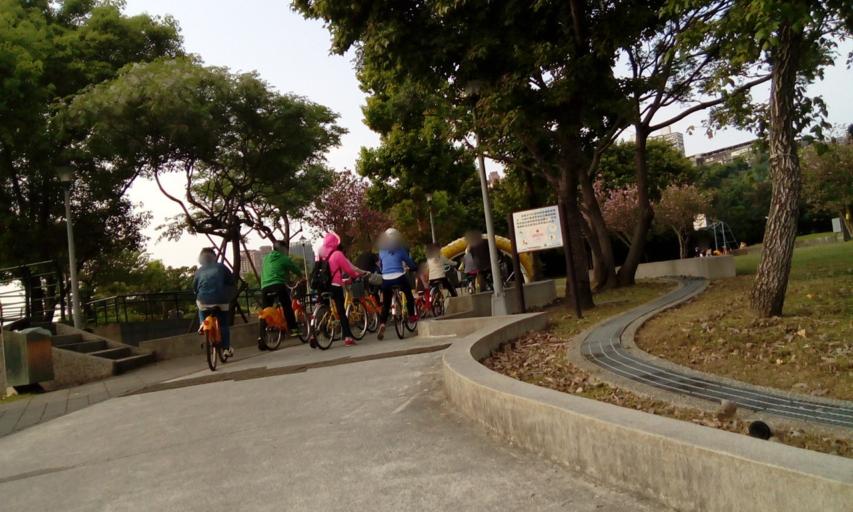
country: TW
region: Taipei
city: Taipei
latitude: 25.1229
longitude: 121.4616
